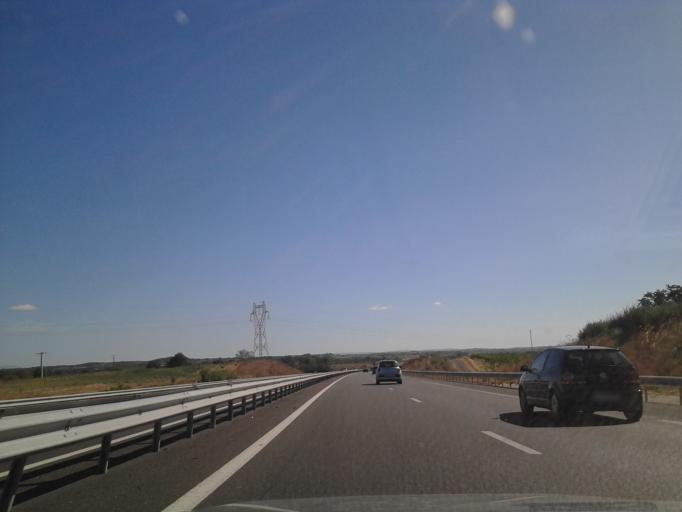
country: FR
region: Languedoc-Roussillon
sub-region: Departement de l'Herault
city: Servian
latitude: 43.3935
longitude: 3.3246
